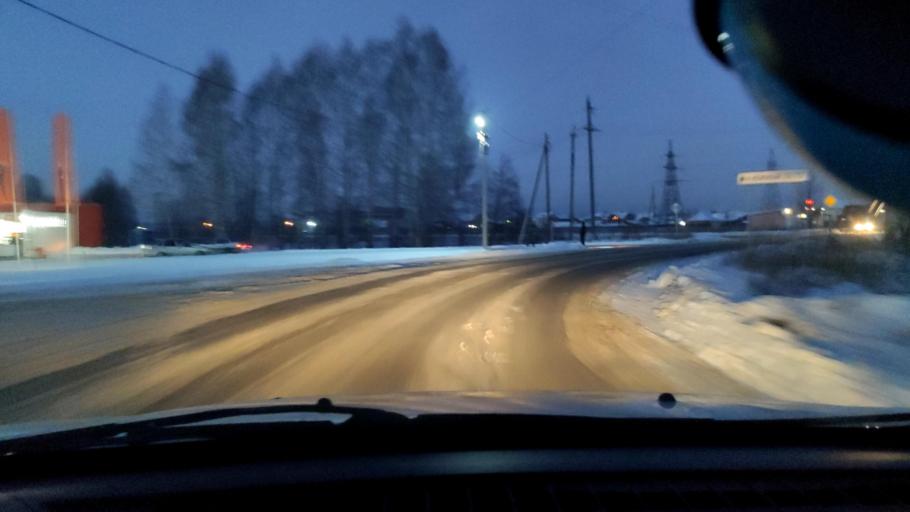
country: RU
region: Perm
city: Kultayevo
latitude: 57.8873
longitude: 55.9235
